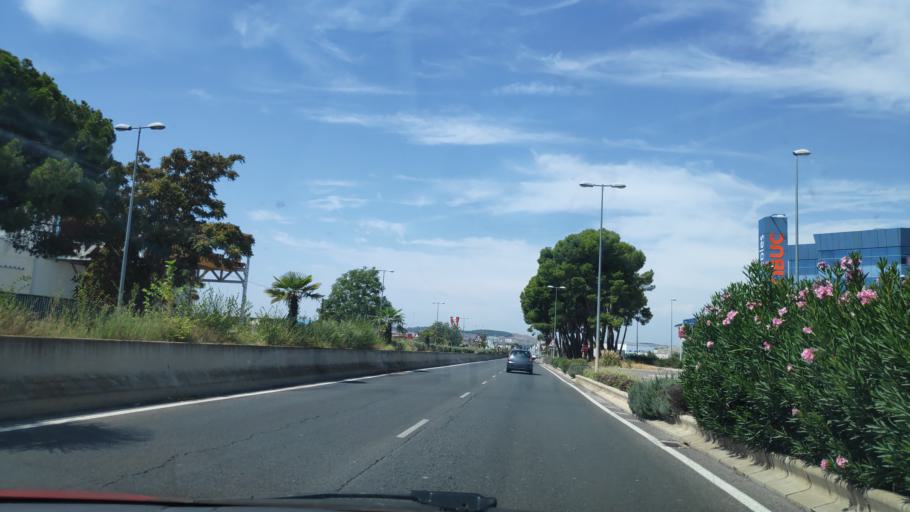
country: ES
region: Madrid
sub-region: Provincia de Madrid
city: Arganda
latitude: 40.3081
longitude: -3.4718
